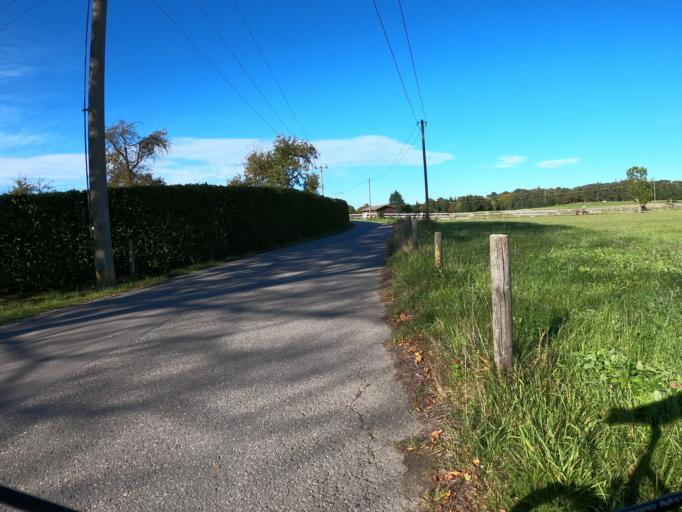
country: DE
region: Bavaria
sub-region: Swabia
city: Nersingen
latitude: 48.4192
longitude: 10.1408
